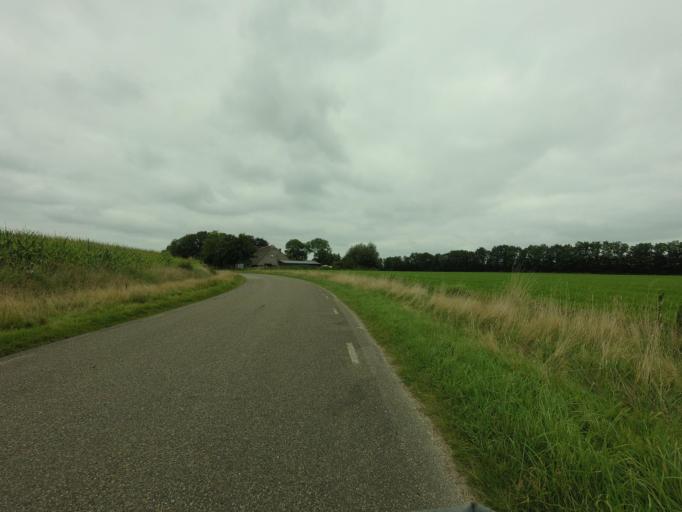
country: NL
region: Overijssel
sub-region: Gemeente Steenwijkerland
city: Steenwijkerwold
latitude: 52.7972
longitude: 6.0476
